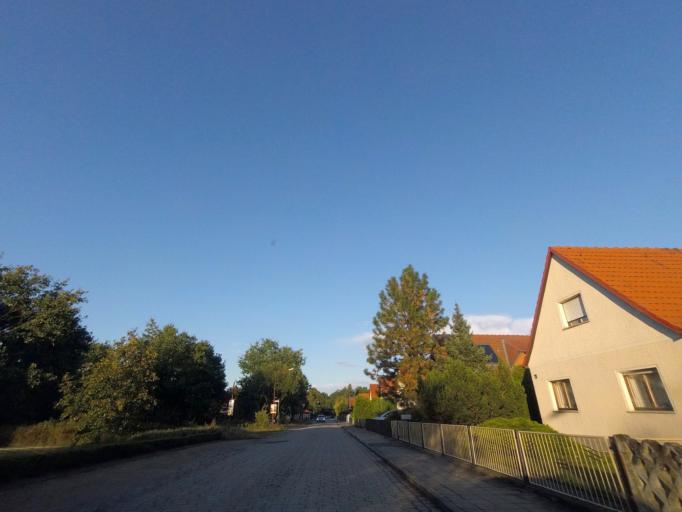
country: DE
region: Brandenburg
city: Treuenbrietzen
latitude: 52.0550
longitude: 12.9009
